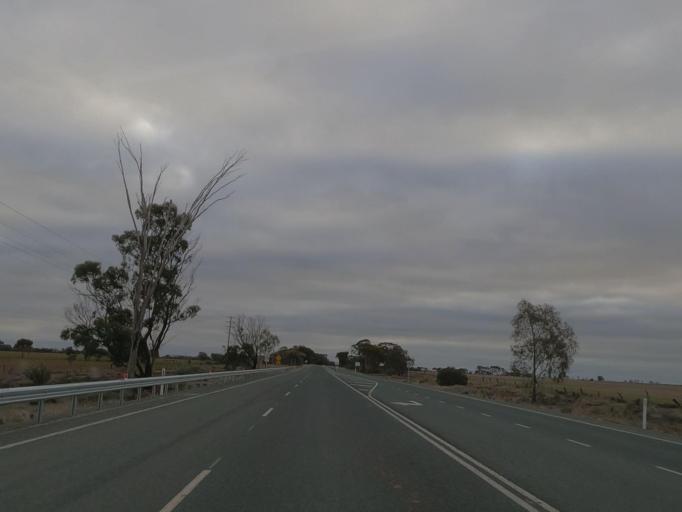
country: AU
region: Victoria
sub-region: Swan Hill
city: Swan Hill
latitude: -35.5507
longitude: 143.7686
